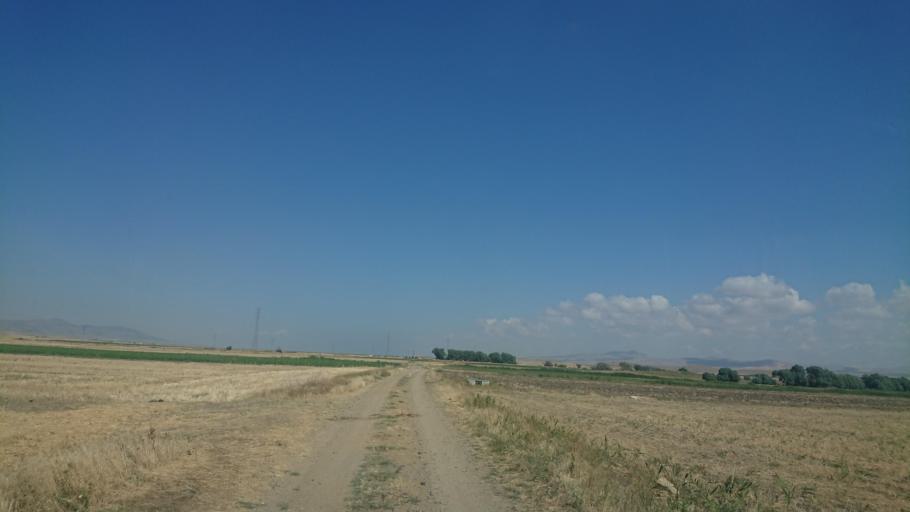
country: TR
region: Aksaray
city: Sariyahsi
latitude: 38.9910
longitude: 33.8993
